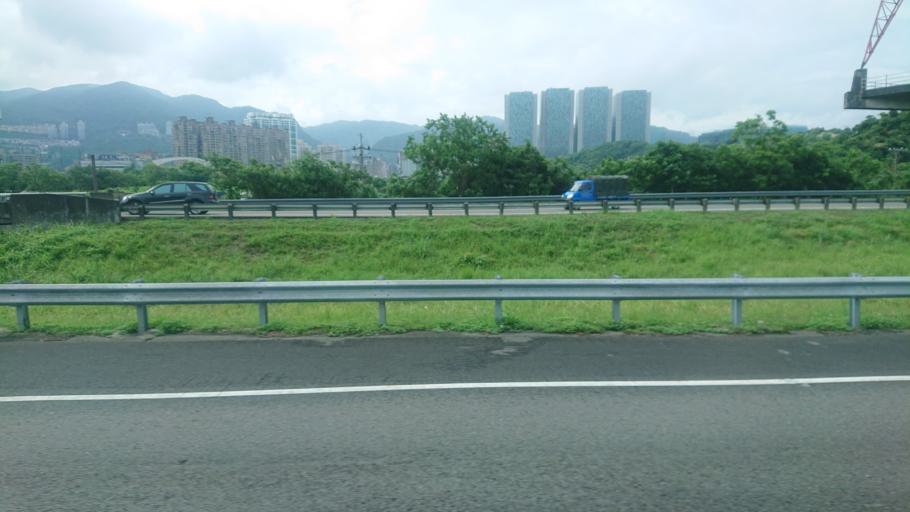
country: TW
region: Taiwan
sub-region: Keelung
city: Keelung
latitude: 25.0730
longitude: 121.6492
